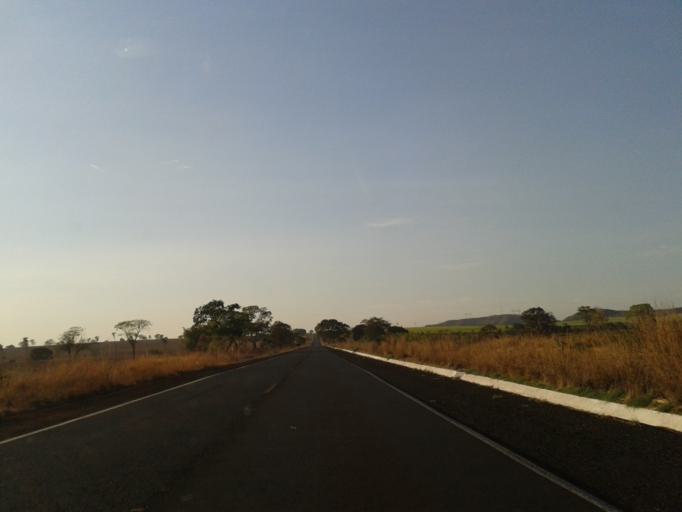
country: BR
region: Minas Gerais
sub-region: Santa Vitoria
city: Santa Vitoria
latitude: -19.1069
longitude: -50.3232
